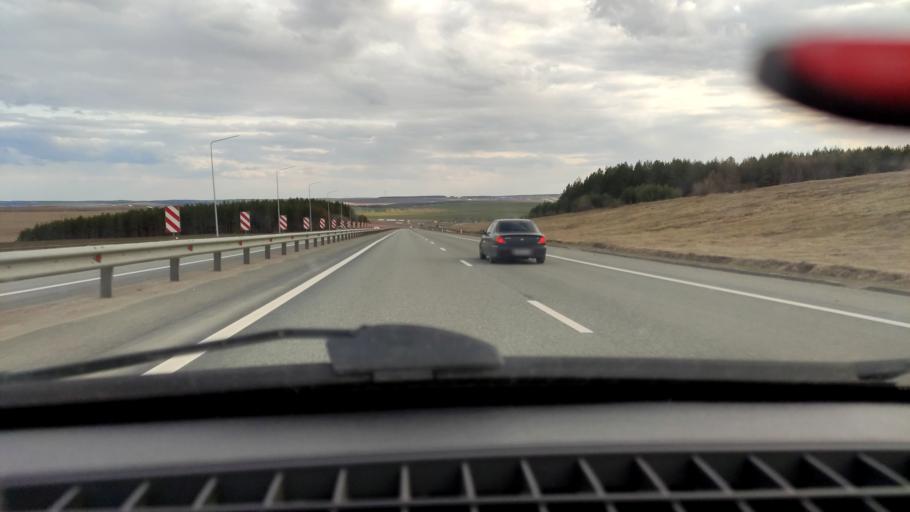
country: RU
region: Bashkortostan
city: Tolbazy
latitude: 54.0944
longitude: 55.8990
